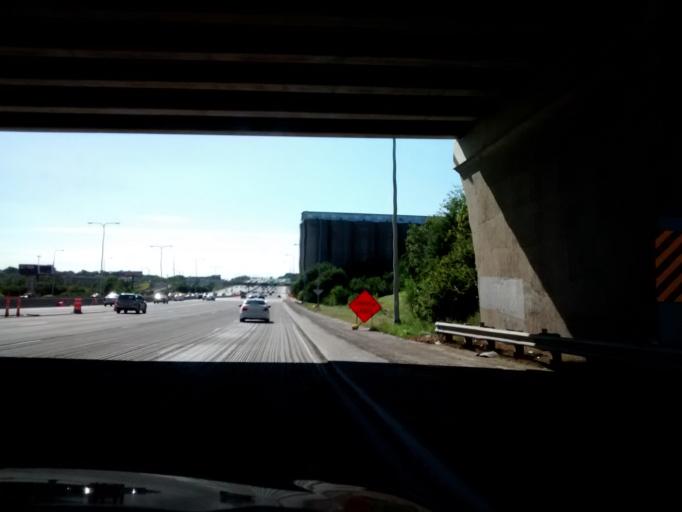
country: US
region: Nebraska
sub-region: Douglas County
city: Omaha
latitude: 41.2276
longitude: -95.9599
